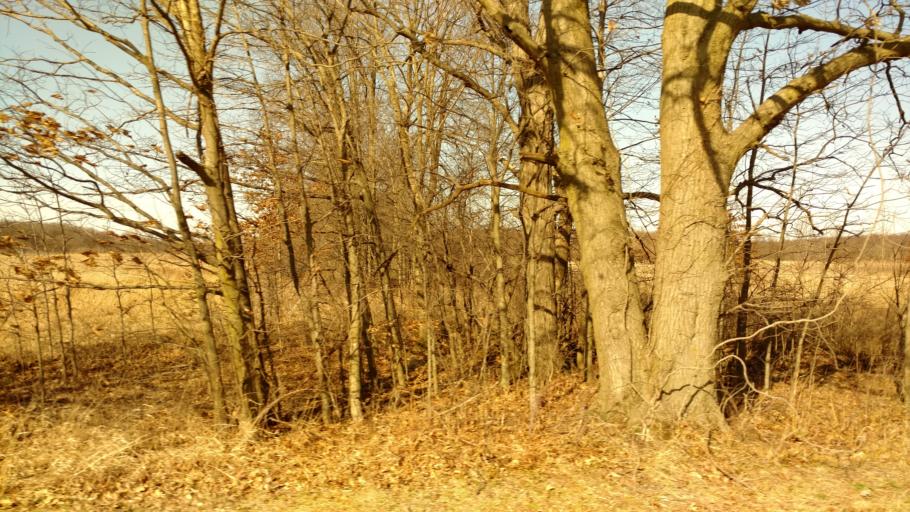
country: US
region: Ohio
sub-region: Wyandot County
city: Upper Sandusky
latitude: 40.6945
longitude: -83.3671
